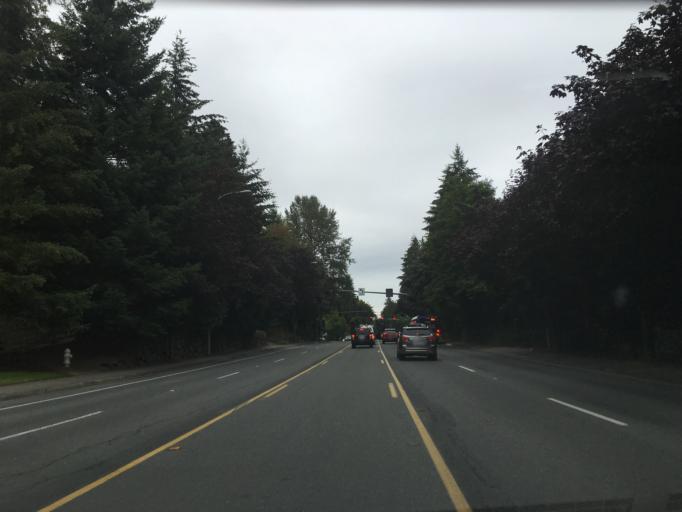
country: US
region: Washington
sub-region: King County
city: Inglewood-Finn Hill
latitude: 47.7126
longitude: -122.2078
